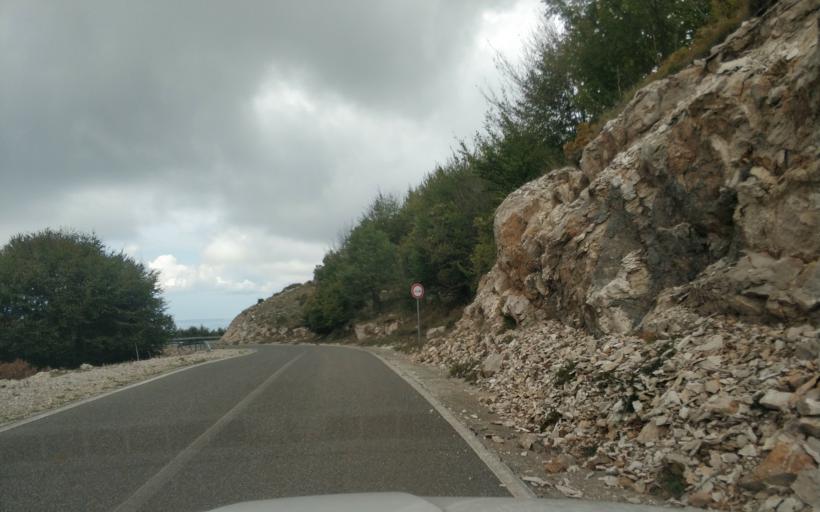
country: AL
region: Durres
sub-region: Rrethi i Krujes
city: Kruje
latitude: 41.5189
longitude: 19.8075
